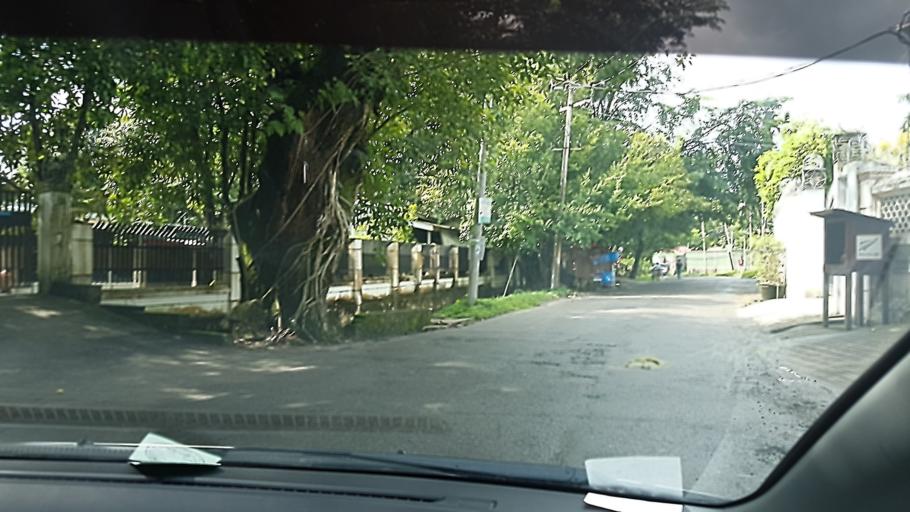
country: MM
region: Yangon
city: Yangon
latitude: 16.8129
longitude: 96.1485
